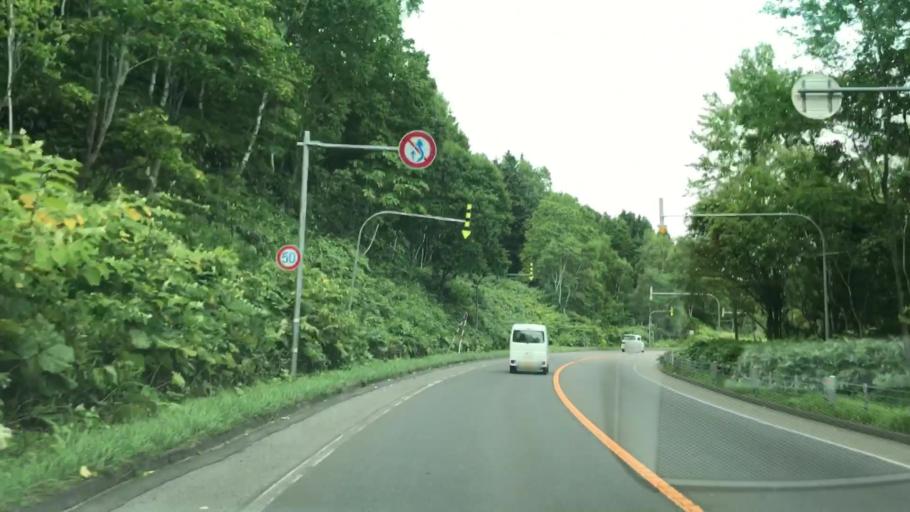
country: JP
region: Hokkaido
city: Niseko Town
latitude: 42.9281
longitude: 140.7153
